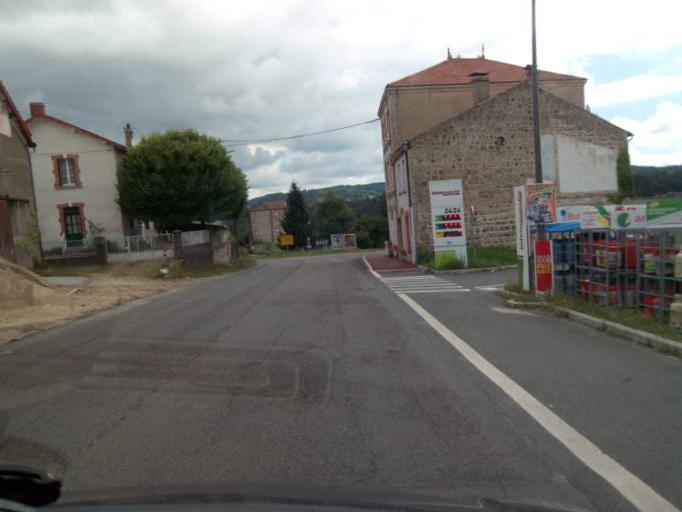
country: FR
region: Rhone-Alpes
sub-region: Departement de la Loire
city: Usson-en-Forez
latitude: 45.3906
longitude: 3.9461
